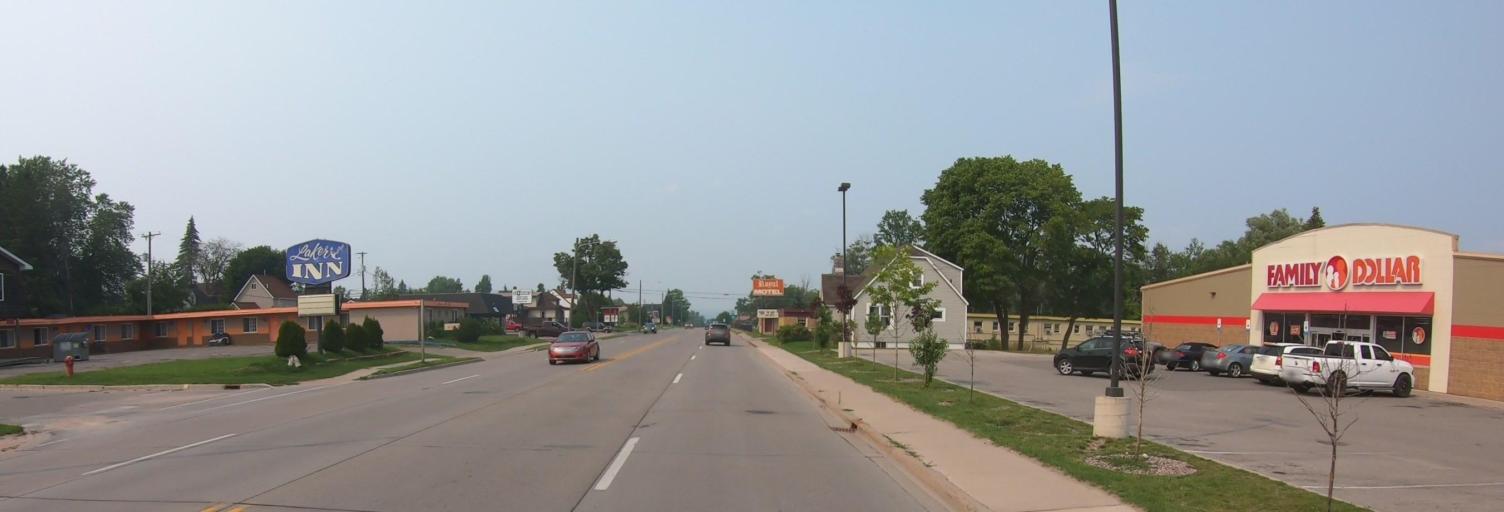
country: US
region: Michigan
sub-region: Chippewa County
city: Sault Ste. Marie
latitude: 46.4835
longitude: -84.3536
